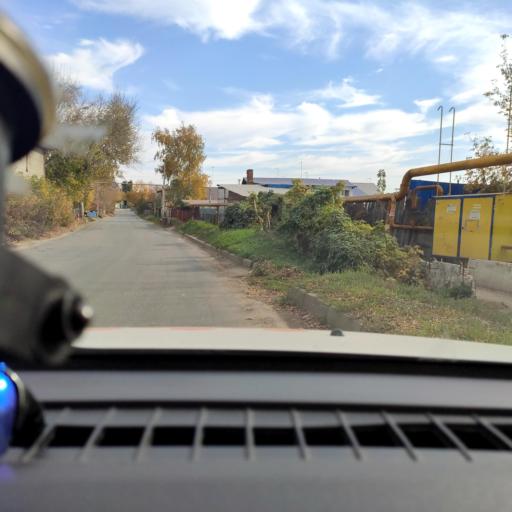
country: RU
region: Samara
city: Samara
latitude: 53.1772
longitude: 50.1479
